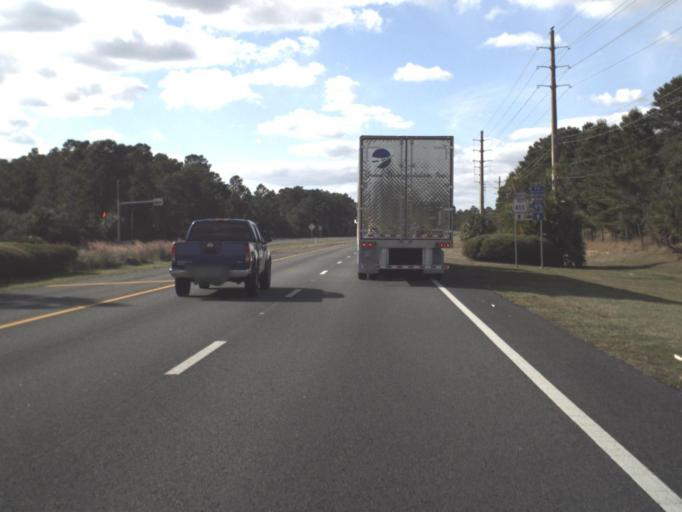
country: US
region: Florida
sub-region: Brevard County
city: Port Saint John
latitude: 28.5327
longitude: -80.8193
